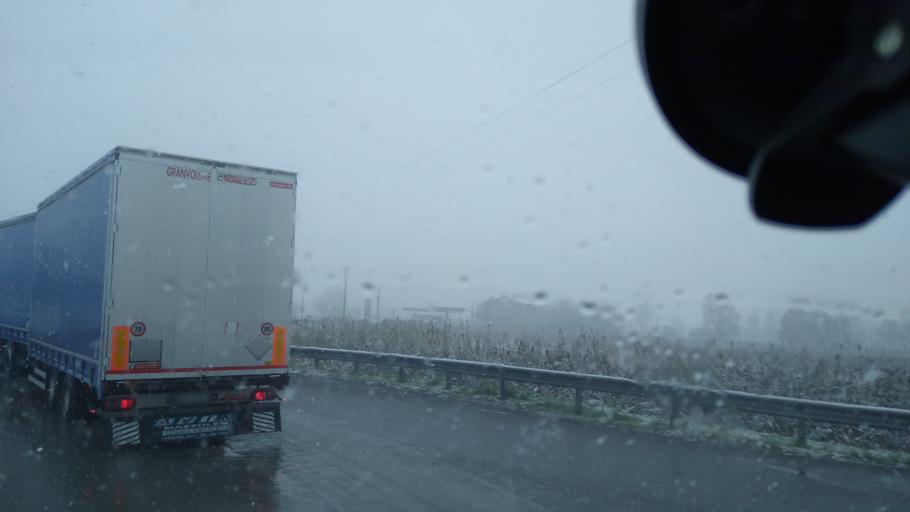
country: IT
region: Lombardy
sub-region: Provincia di Bergamo
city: Spirano
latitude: 45.5931
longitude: 9.6660
